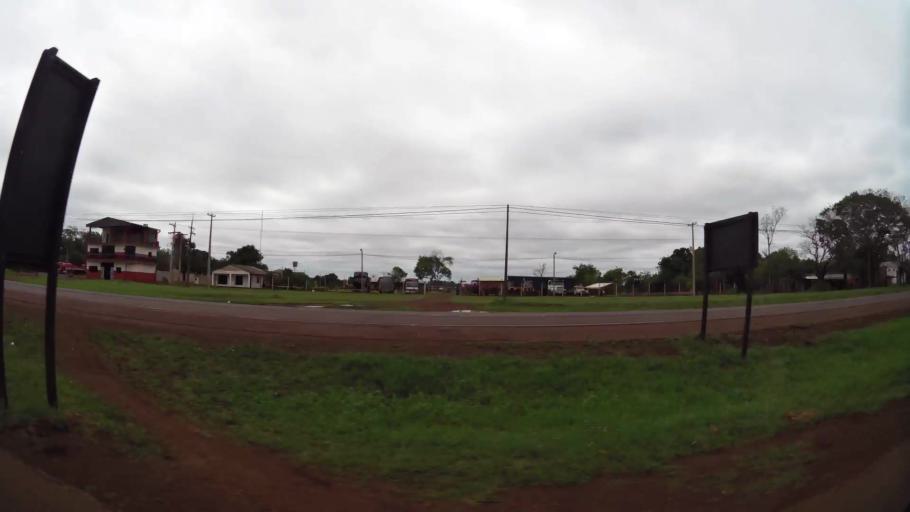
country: PY
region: Alto Parana
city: Colonia Yguazu
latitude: -25.4887
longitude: -54.8132
